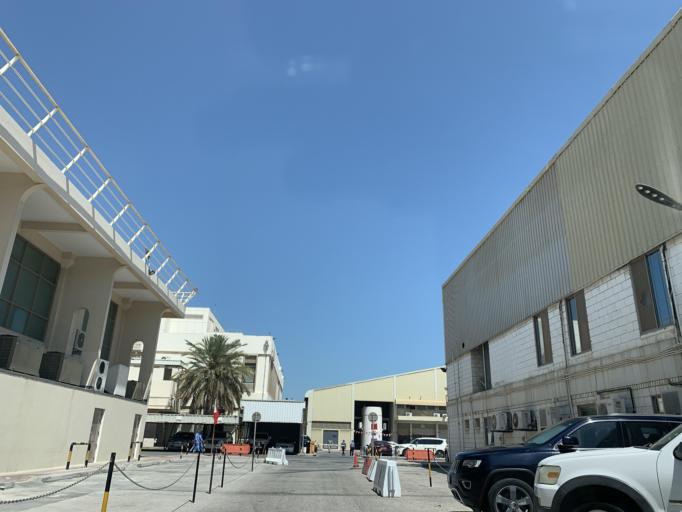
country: BH
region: Manama
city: Manama
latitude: 26.2149
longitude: 50.5733
